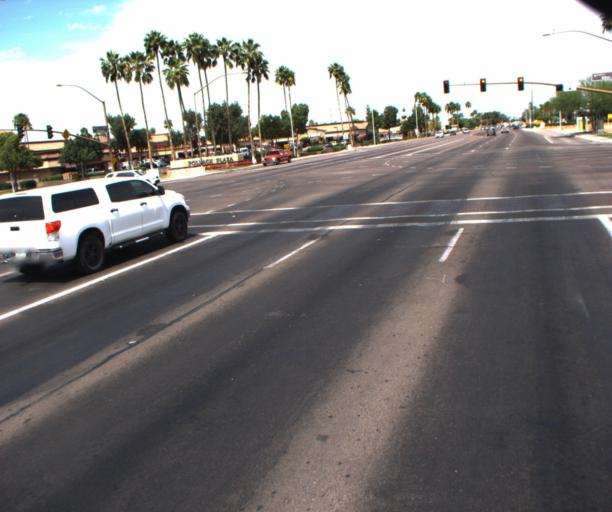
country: US
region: Arizona
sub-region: Maricopa County
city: San Carlos
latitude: 33.3493
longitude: -111.8416
